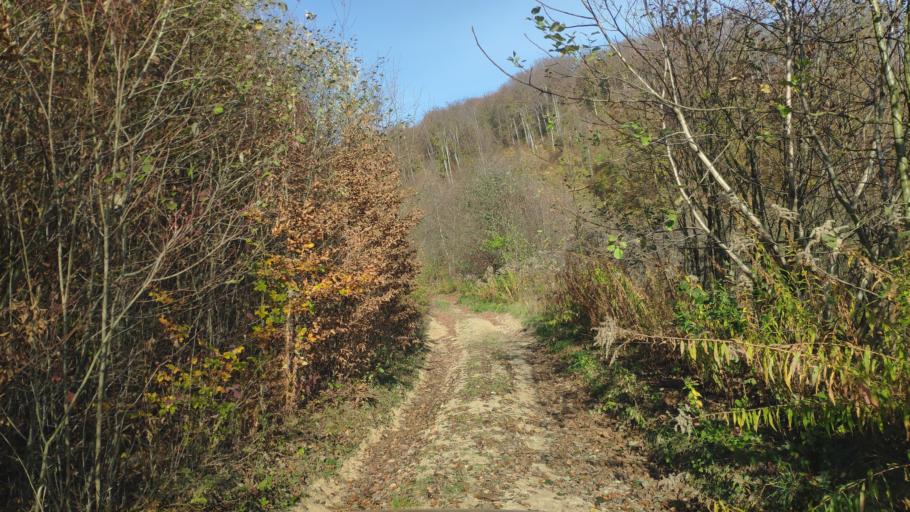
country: SK
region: Presovsky
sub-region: Okres Presov
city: Presov
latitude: 48.9024
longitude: 21.2220
